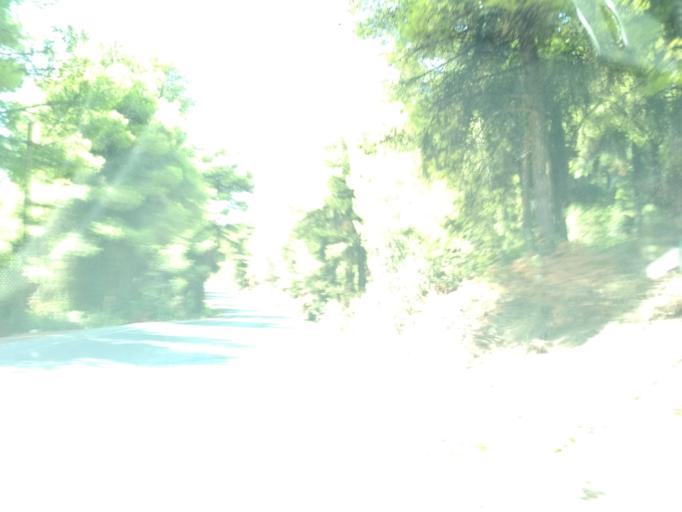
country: GR
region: Central Greece
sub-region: Nomos Evvoias
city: Roviai
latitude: 38.8222
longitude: 23.2404
